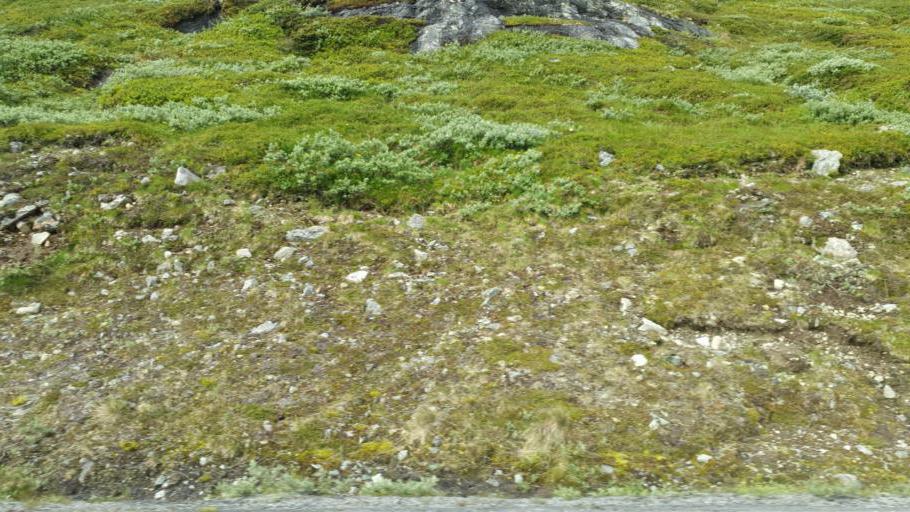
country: NO
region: Oppland
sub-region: Vestre Slidre
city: Slidre
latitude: 61.3408
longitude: 8.8135
